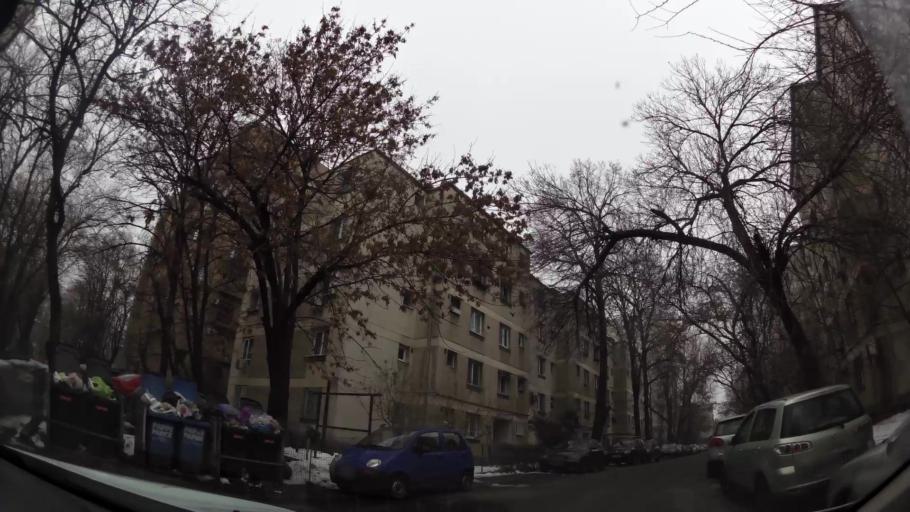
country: RO
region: Bucuresti
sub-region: Municipiul Bucuresti
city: Bucharest
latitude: 44.4270
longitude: 26.1262
